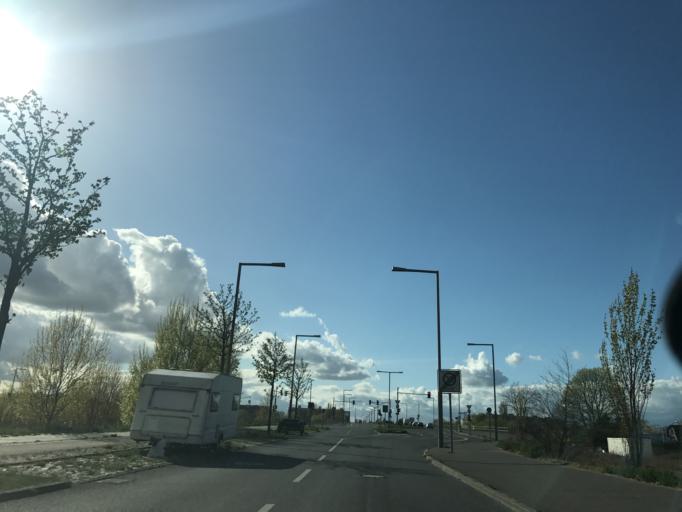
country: DE
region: Berlin
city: Haselhorst
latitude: 52.5586
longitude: 13.2296
